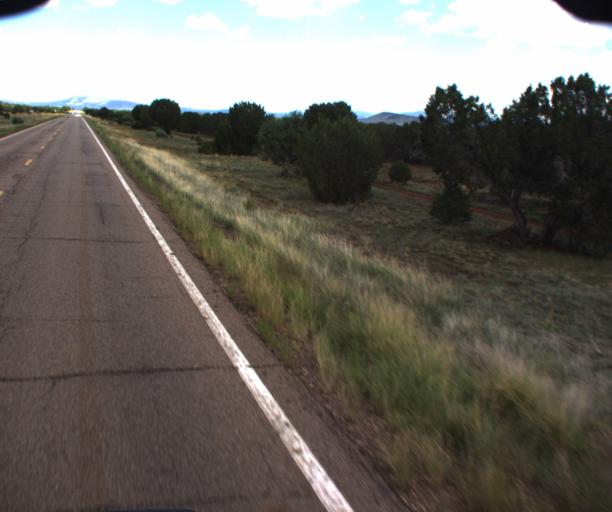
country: US
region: Arizona
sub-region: Navajo County
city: Pinetop-Lakeside
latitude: 34.2725
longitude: -109.7535
